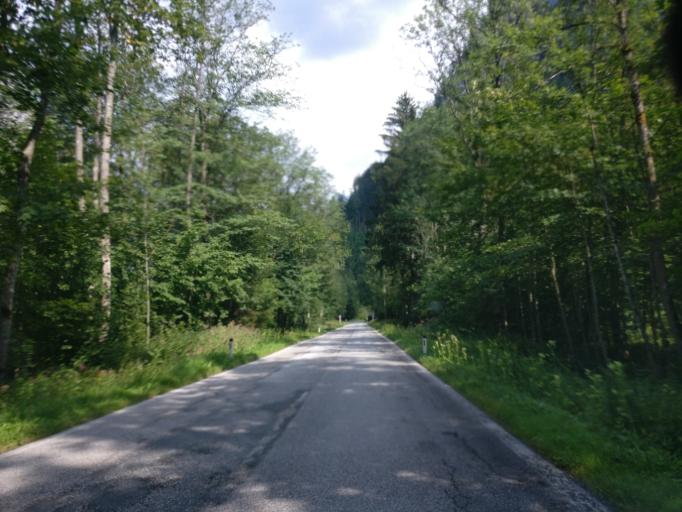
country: AT
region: Styria
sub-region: Politischer Bezirk Liezen
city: Johnsbach
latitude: 47.5810
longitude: 14.5435
